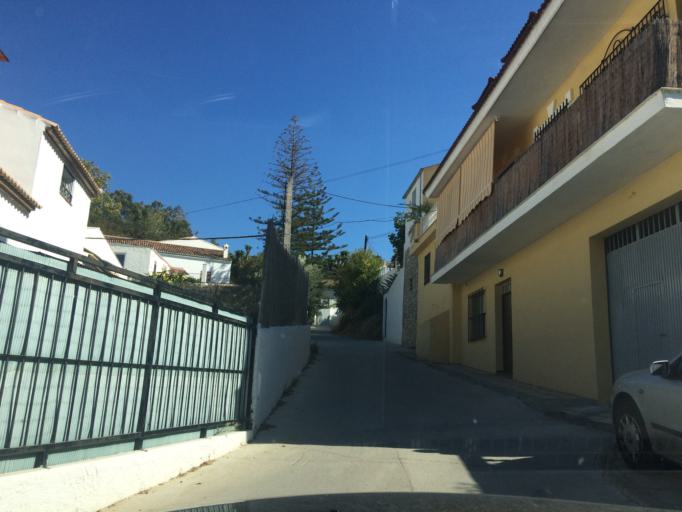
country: ES
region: Andalusia
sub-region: Provincia de Malaga
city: Malaga
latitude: 36.7631
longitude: -4.4217
